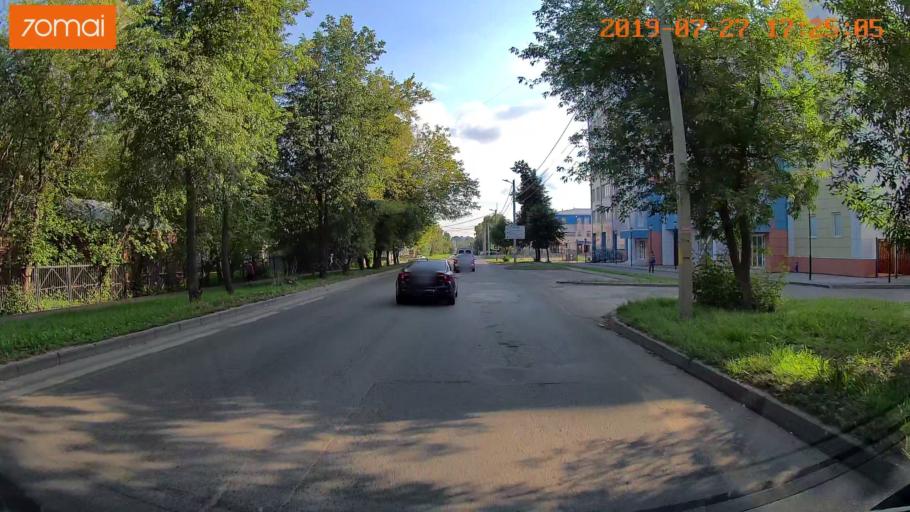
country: RU
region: Ivanovo
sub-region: Gorod Ivanovo
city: Ivanovo
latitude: 57.0184
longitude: 40.9583
